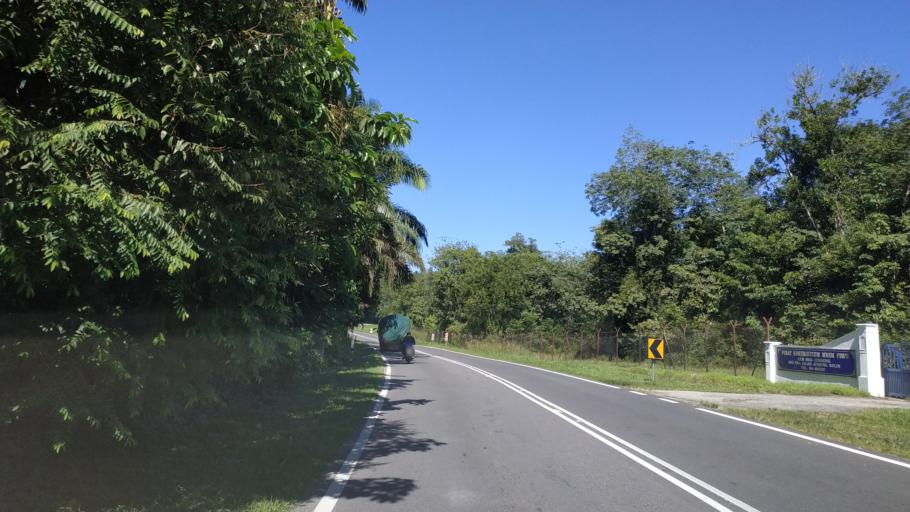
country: MY
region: Kedah
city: Kulim
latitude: 5.3233
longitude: 100.5363
